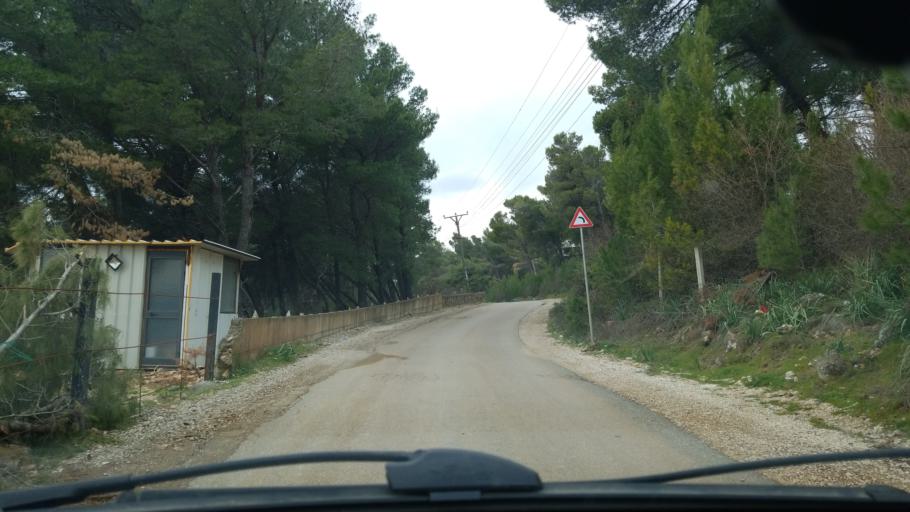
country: AL
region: Lezhe
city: Shengjin
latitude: 41.8114
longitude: 19.5811
